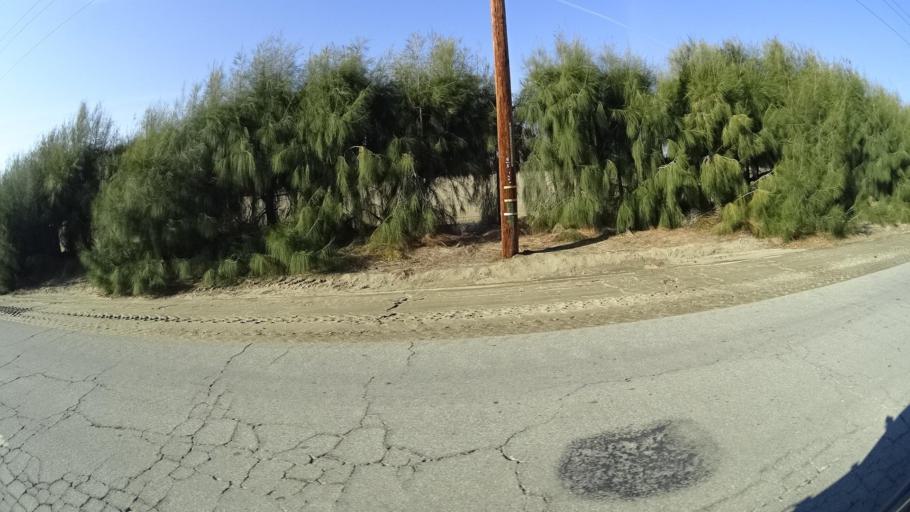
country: US
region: California
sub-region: Kern County
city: Arvin
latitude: 35.1379
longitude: -118.8777
